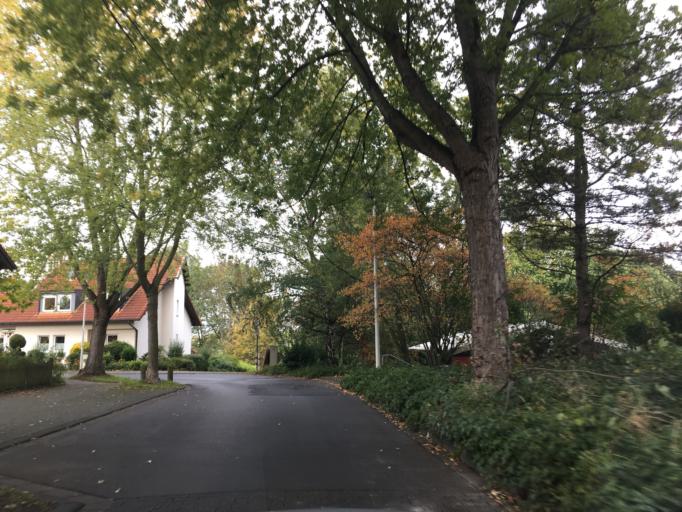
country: DE
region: North Rhine-Westphalia
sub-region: Regierungsbezirk Koln
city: Bonn
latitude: 50.7526
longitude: 7.1169
